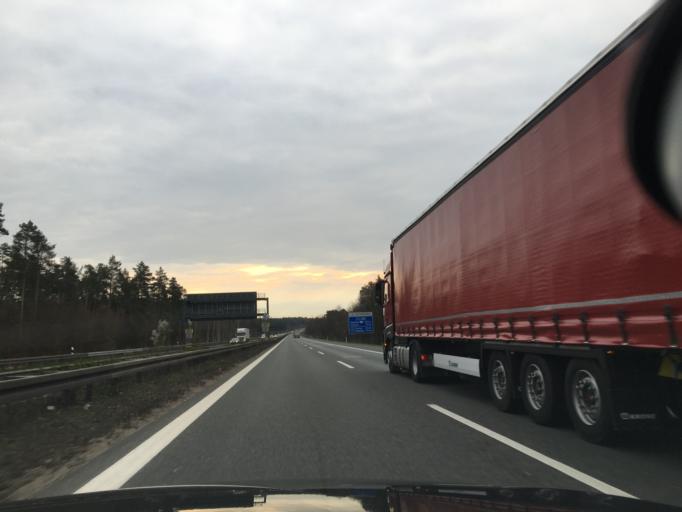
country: DE
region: Bavaria
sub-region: Regierungsbezirk Mittelfranken
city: Feucht
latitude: 49.3982
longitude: 11.2135
